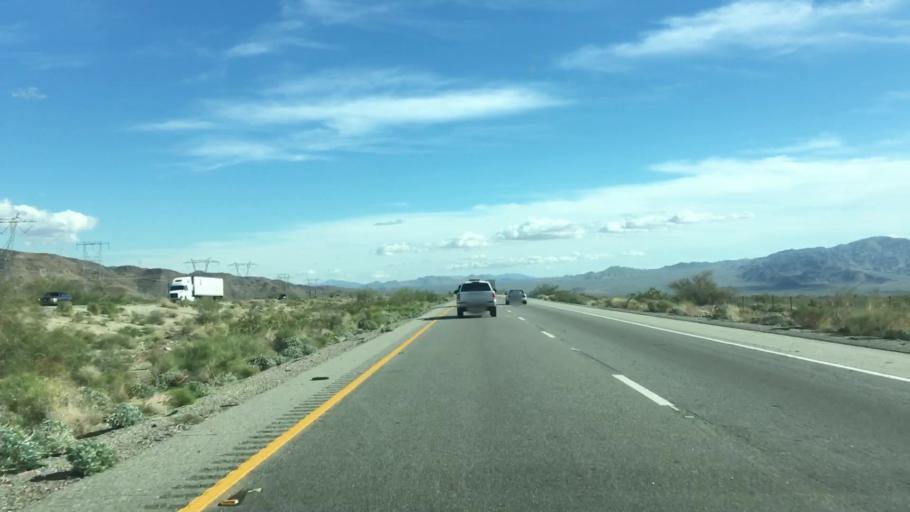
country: US
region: California
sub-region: Riverside County
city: Mecca
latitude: 33.6774
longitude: -115.9594
